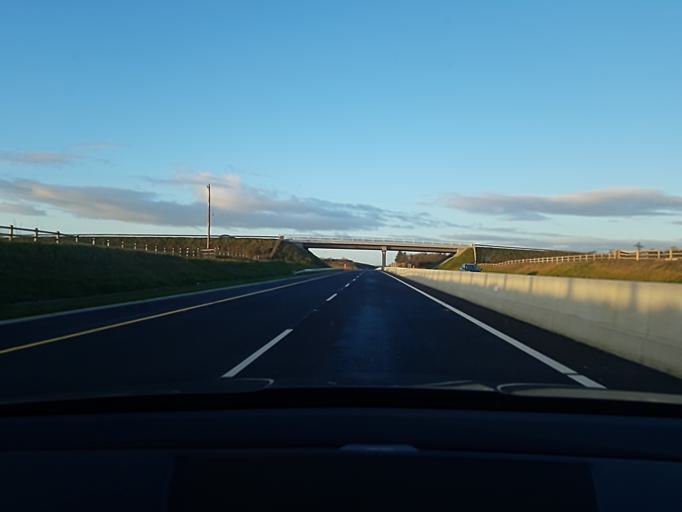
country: IE
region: Connaught
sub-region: County Galway
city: Athenry
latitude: 53.3371
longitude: -8.8022
